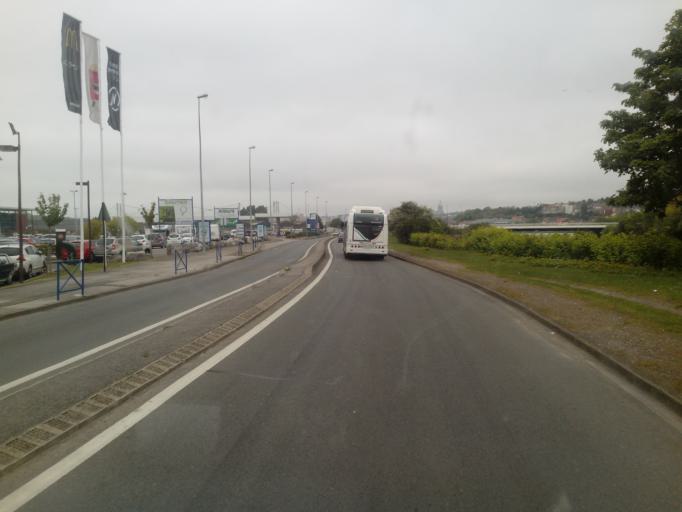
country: FR
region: Nord-Pas-de-Calais
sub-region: Departement du Pas-de-Calais
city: Boulogne-sur-Mer
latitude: 50.7001
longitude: 1.6091
